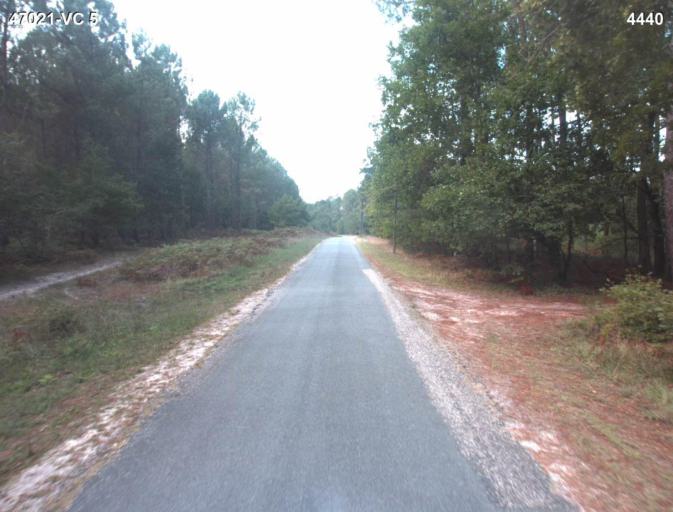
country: FR
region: Aquitaine
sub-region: Departement du Lot-et-Garonne
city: Barbaste
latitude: 44.1449
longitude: 0.2446
